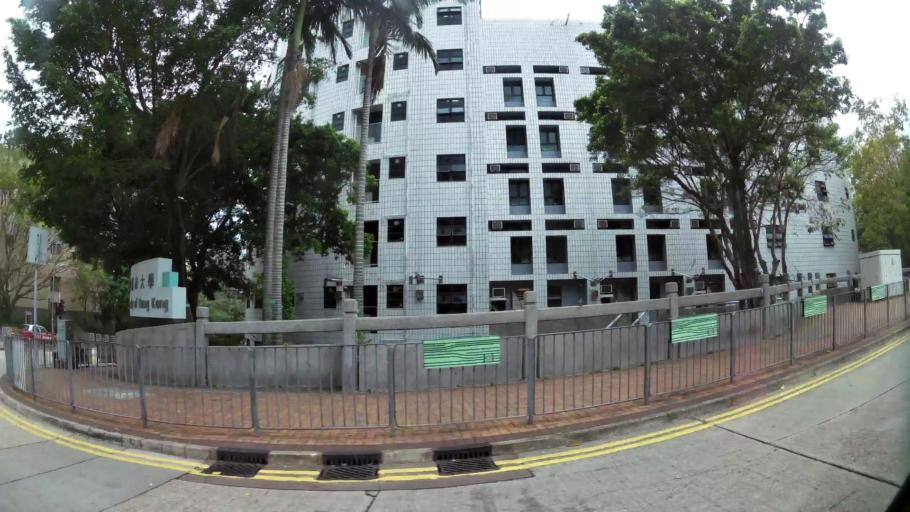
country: HK
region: Wong Tai Sin
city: Wong Tai Sin
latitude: 22.3364
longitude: 114.1749
